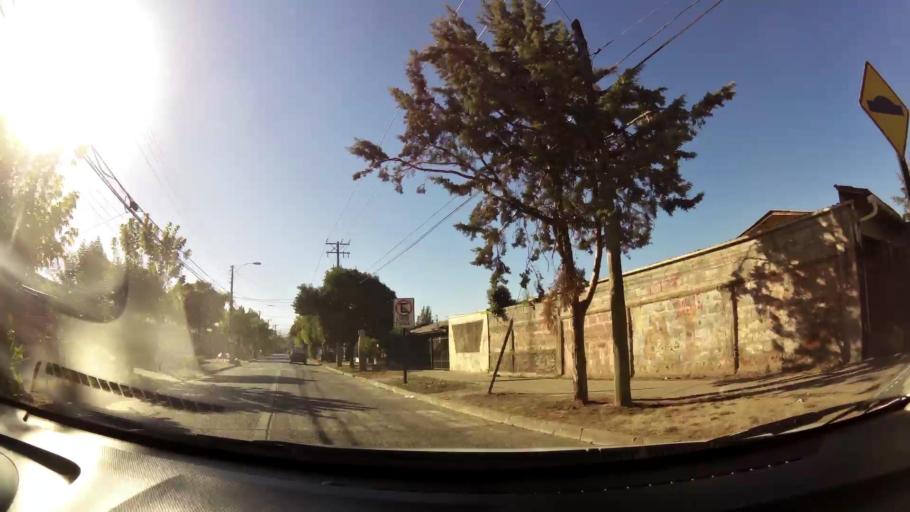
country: CL
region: O'Higgins
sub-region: Provincia de Cachapoal
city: Rancagua
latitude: -34.1845
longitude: -70.7293
